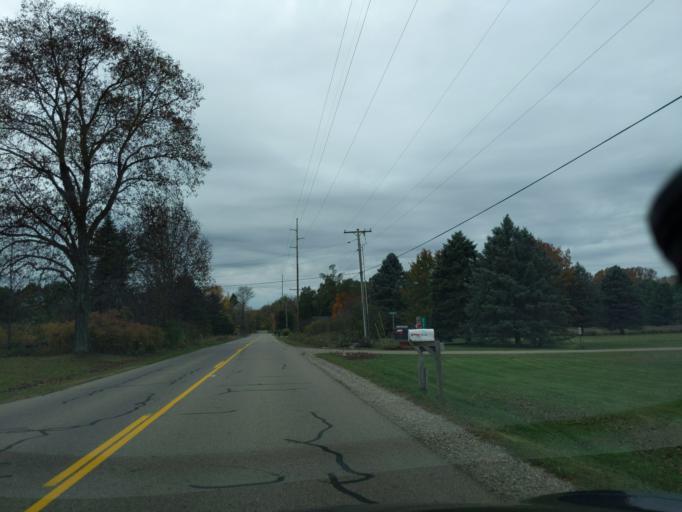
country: US
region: Michigan
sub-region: Eaton County
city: Eaton Rapids
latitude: 42.5239
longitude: -84.6374
